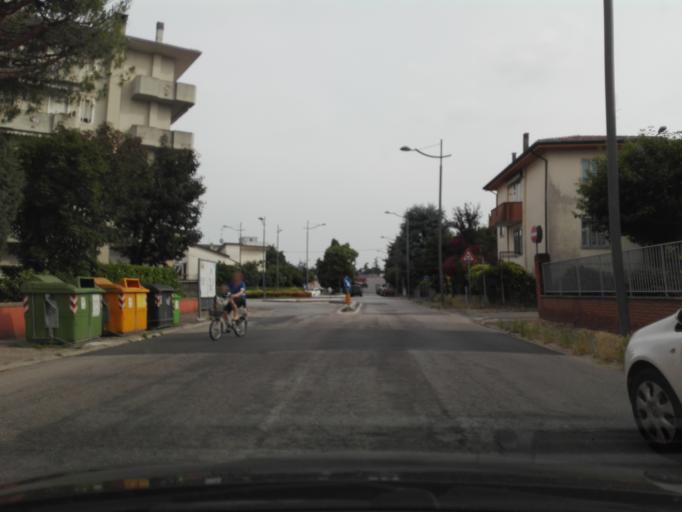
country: IT
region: Veneto
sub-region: Provincia di Rovigo
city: Rovigo
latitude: 45.0761
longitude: 11.7980
